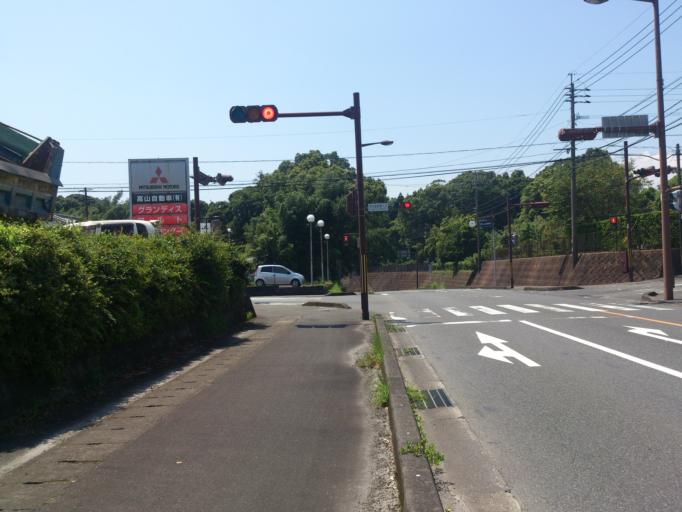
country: JP
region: Kagoshima
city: Kanoya
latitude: 31.3458
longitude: 130.9566
